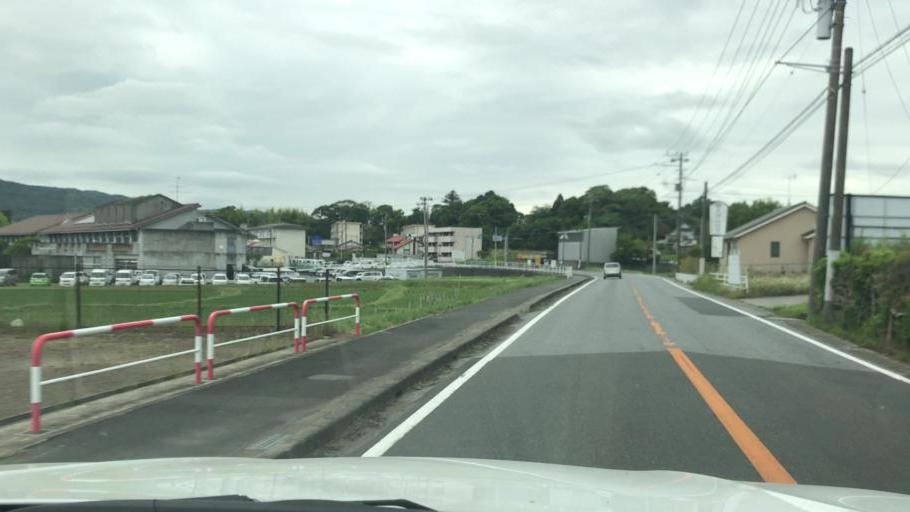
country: JP
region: Chiba
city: Kawaguchi
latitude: 35.1236
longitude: 140.0879
